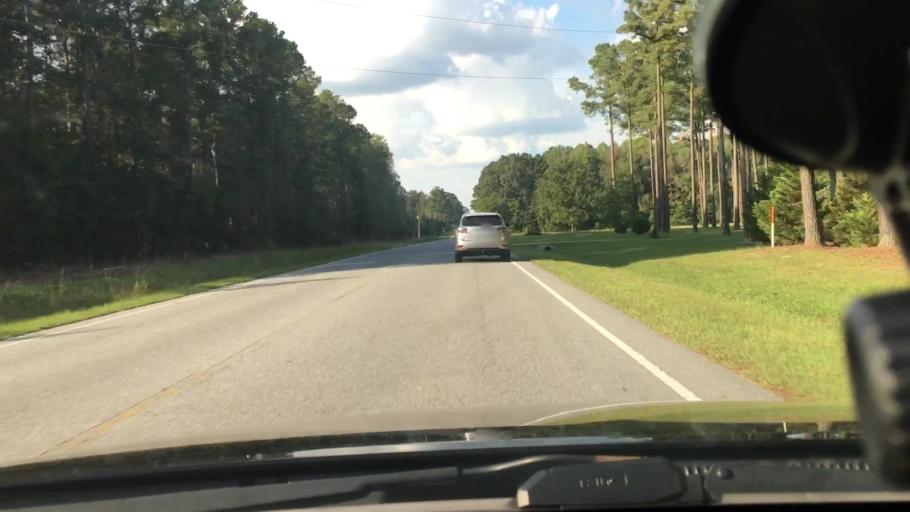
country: US
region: North Carolina
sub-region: Pitt County
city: Windsor
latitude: 35.4420
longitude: -77.2633
